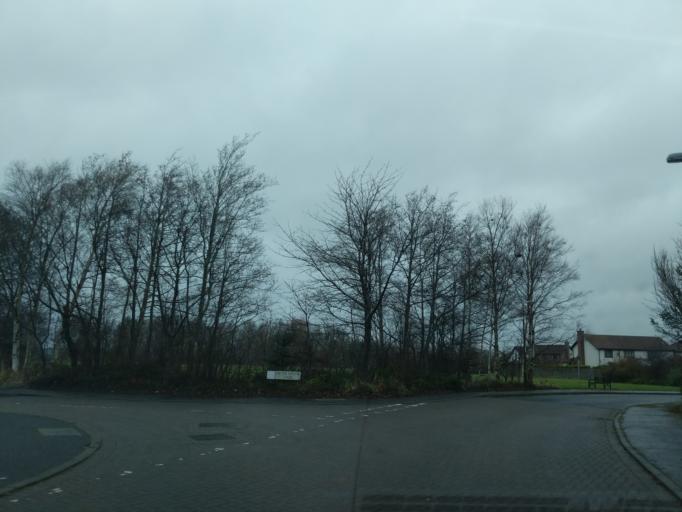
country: GB
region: Scotland
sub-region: Midlothian
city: Loanhead
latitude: 55.9061
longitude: -3.1747
